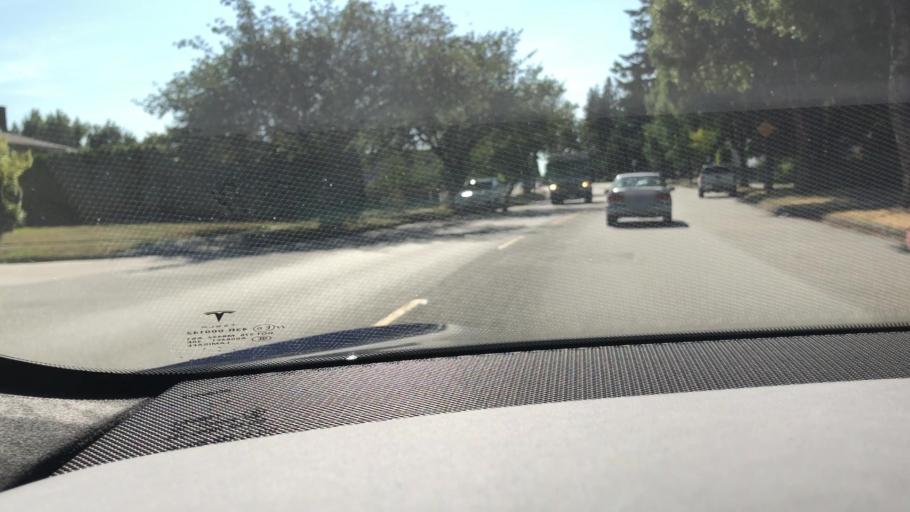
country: CA
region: British Columbia
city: Vancouver
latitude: 49.2245
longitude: -123.0579
